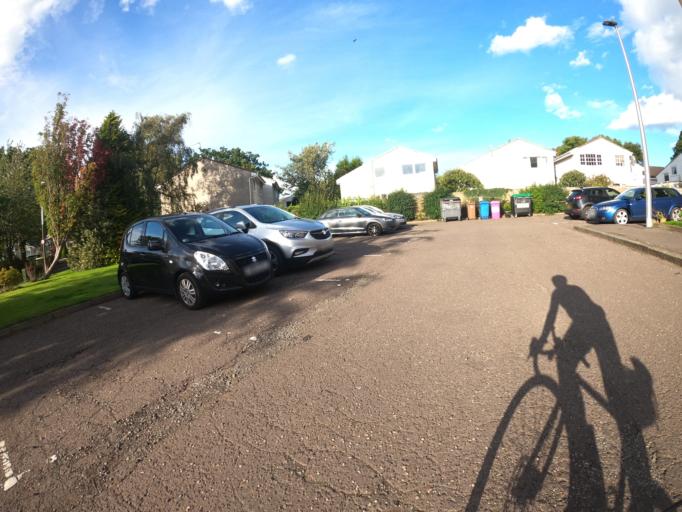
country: GB
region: Scotland
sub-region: Edinburgh
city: Colinton
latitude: 55.9624
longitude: -3.2879
